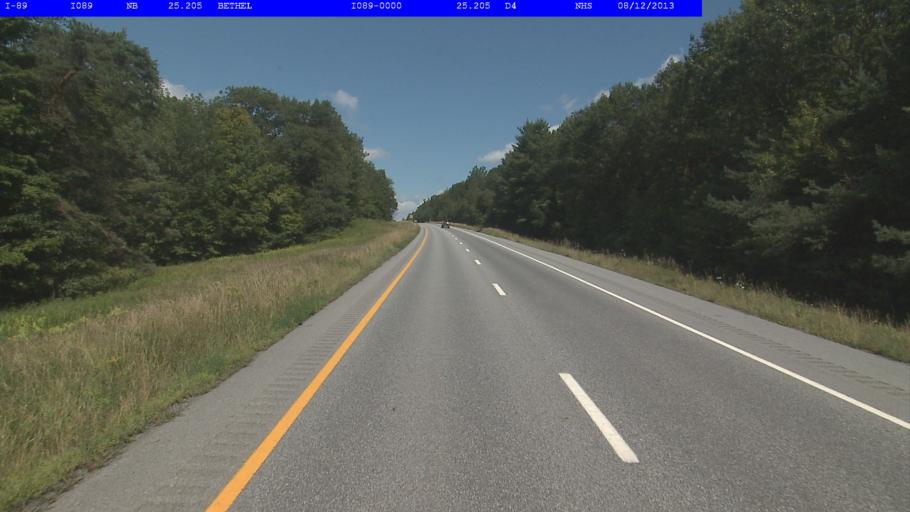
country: US
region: Vermont
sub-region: Orange County
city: Randolph
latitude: 43.8643
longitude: -72.6077
